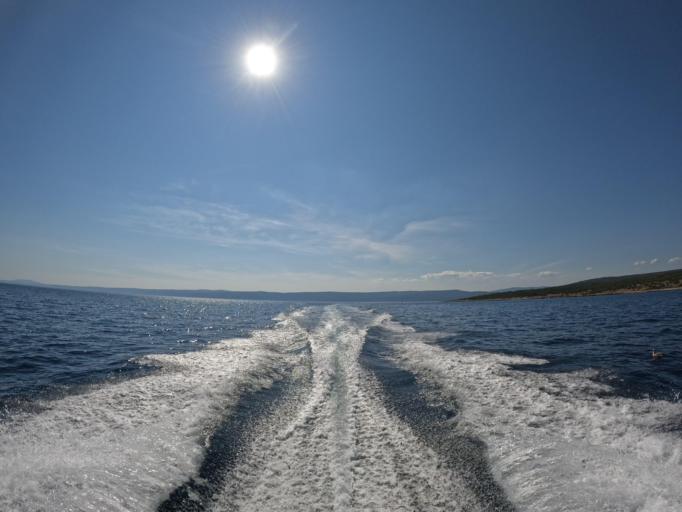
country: HR
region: Primorsko-Goranska
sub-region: Grad Krk
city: Krk
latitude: 44.9517
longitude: 14.5516
